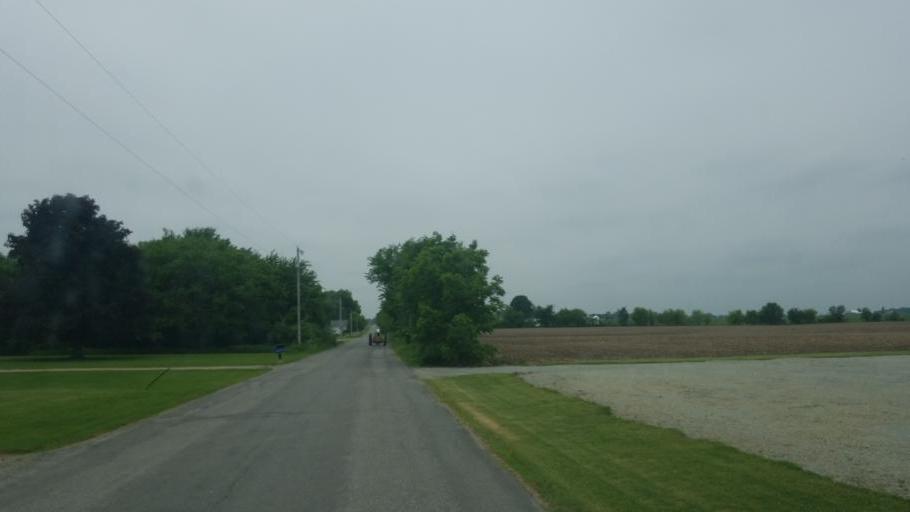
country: US
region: Indiana
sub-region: Elkhart County
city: Nappanee
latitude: 41.4718
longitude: -86.0219
